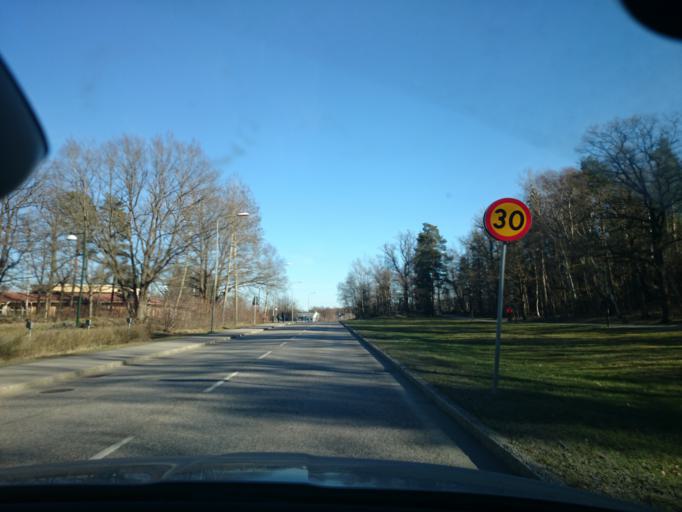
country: SE
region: Stockholm
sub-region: Huddinge Kommun
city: Huddinge
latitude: 59.2772
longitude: 17.9778
